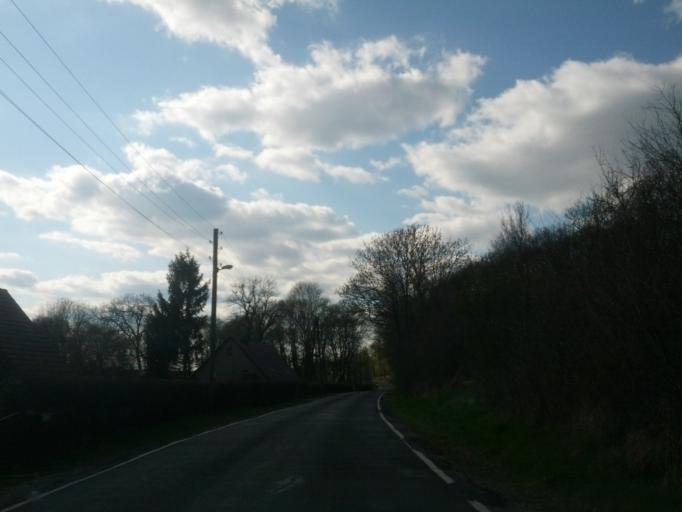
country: DE
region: Thuringia
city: Seebach
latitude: 50.9801
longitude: 10.4364
